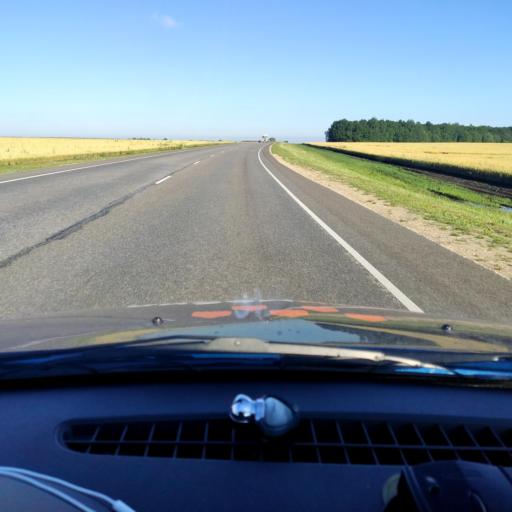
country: RU
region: Orjol
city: Pokrovskoye
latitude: 52.6215
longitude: 36.7288
